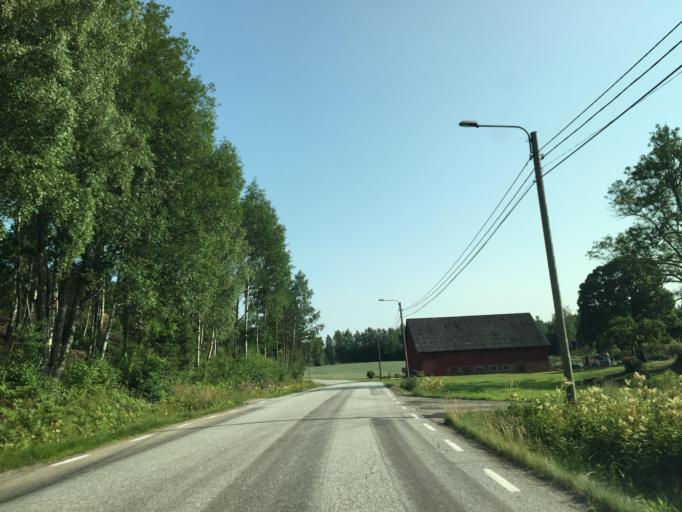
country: SE
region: Vaestra Goetaland
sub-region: Trollhattan
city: Trollhattan
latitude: 58.2937
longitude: 12.2502
